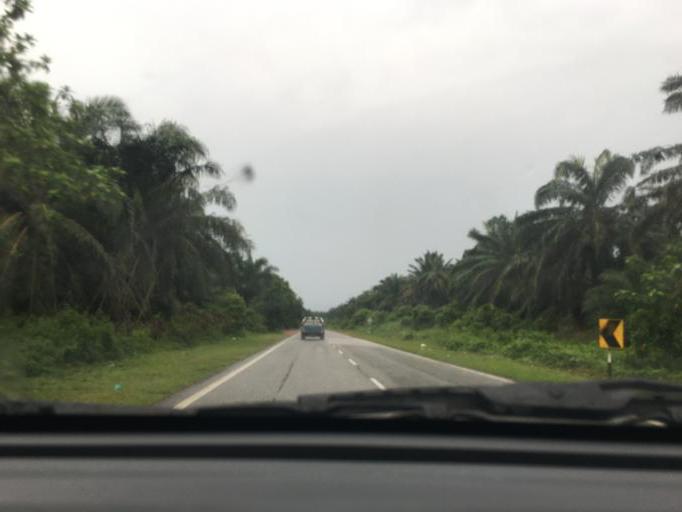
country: MY
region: Kedah
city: Sungai Petani
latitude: 5.6375
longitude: 100.6287
